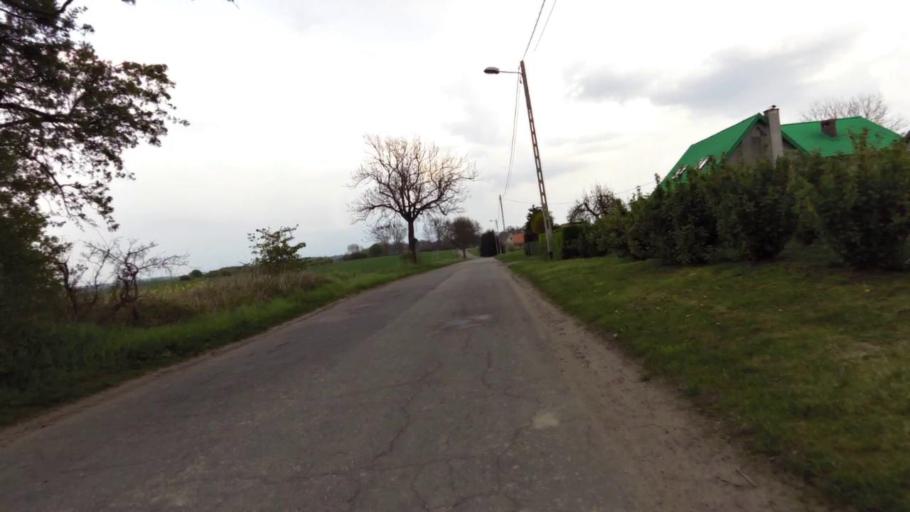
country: PL
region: West Pomeranian Voivodeship
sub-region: Powiat mysliborski
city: Mysliborz
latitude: 52.9145
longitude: 14.8033
